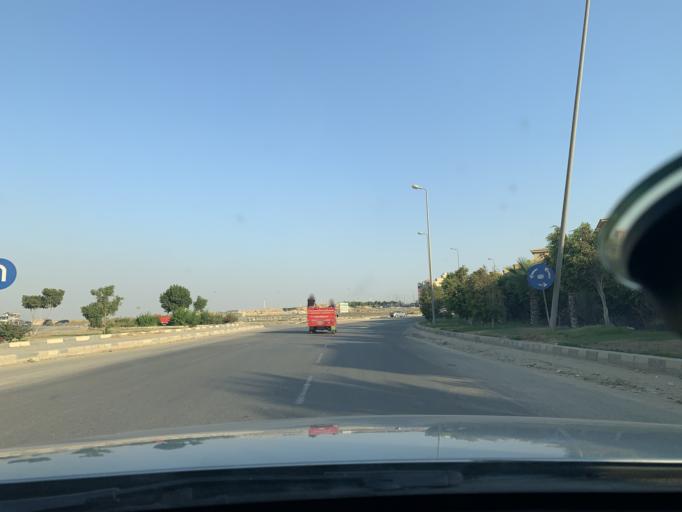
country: EG
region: Muhafazat al Qalyubiyah
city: Al Khankah
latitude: 30.0442
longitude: 31.5217
